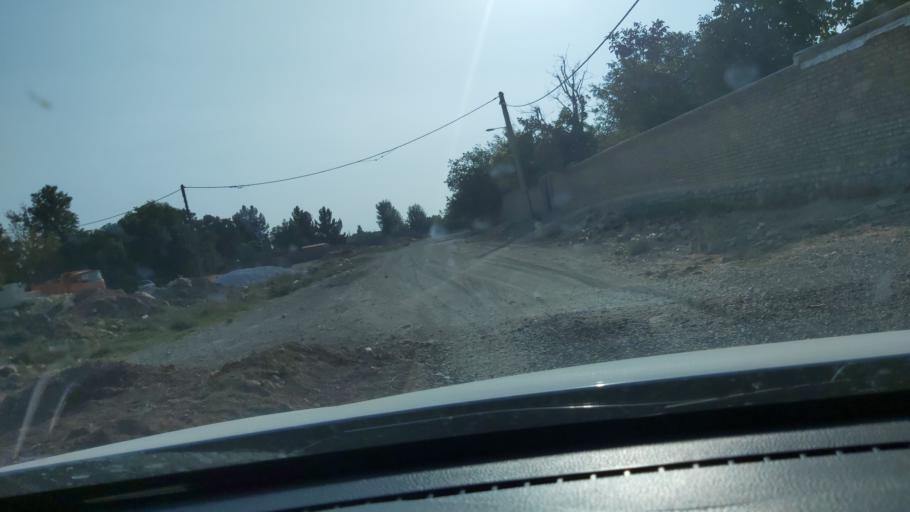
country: IR
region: Alborz
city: Hashtgerd
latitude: 35.9538
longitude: 50.7803
